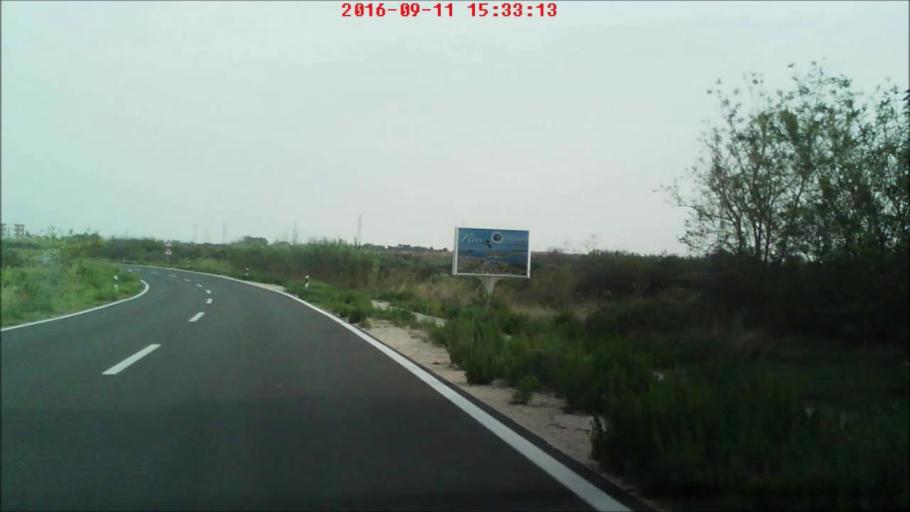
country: HR
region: Zadarska
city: Nin
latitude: 44.2492
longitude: 15.1643
